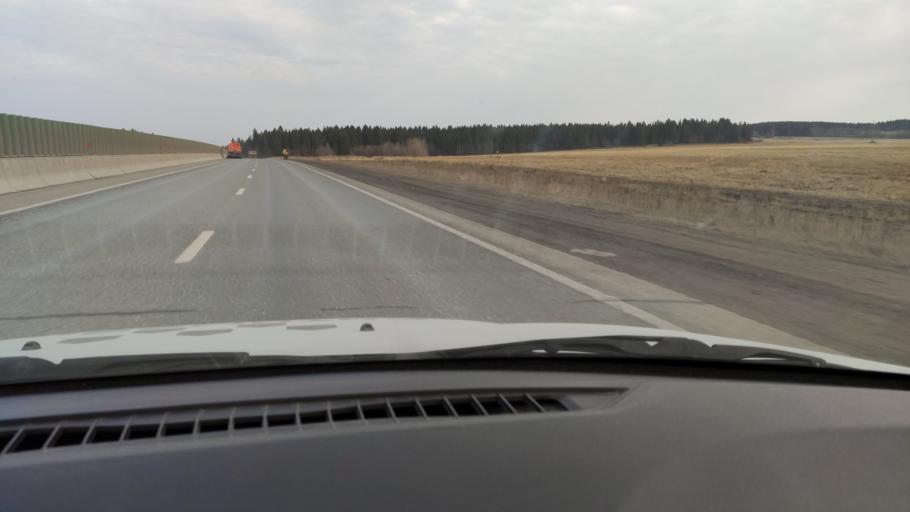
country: RU
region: Perm
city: Ferma
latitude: 57.9402
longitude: 56.3716
